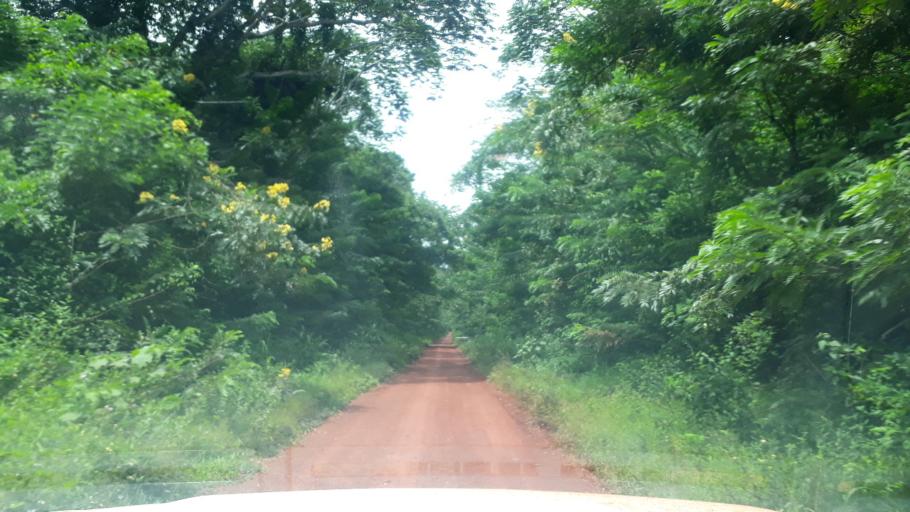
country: CD
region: Eastern Province
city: Aketi
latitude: 2.9278
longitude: 24.0865
